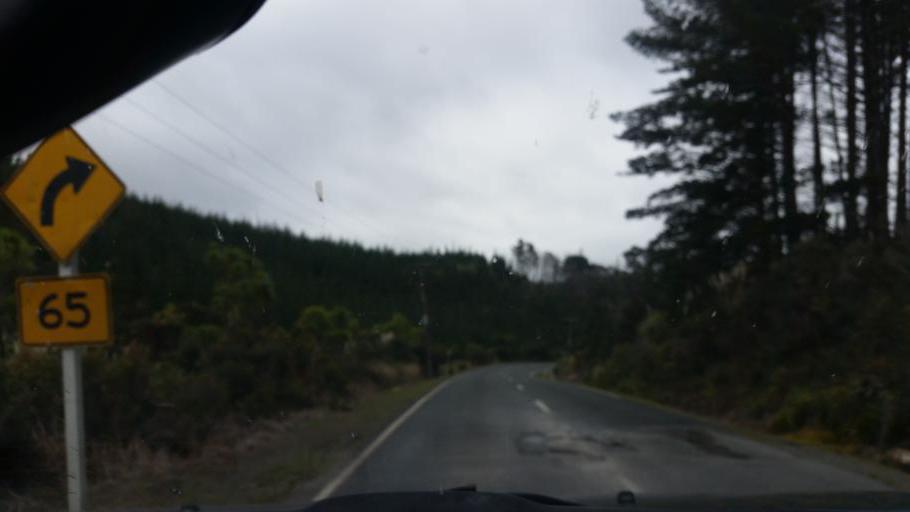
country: NZ
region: Northland
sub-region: Kaipara District
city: Dargaville
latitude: -35.8195
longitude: 173.7108
